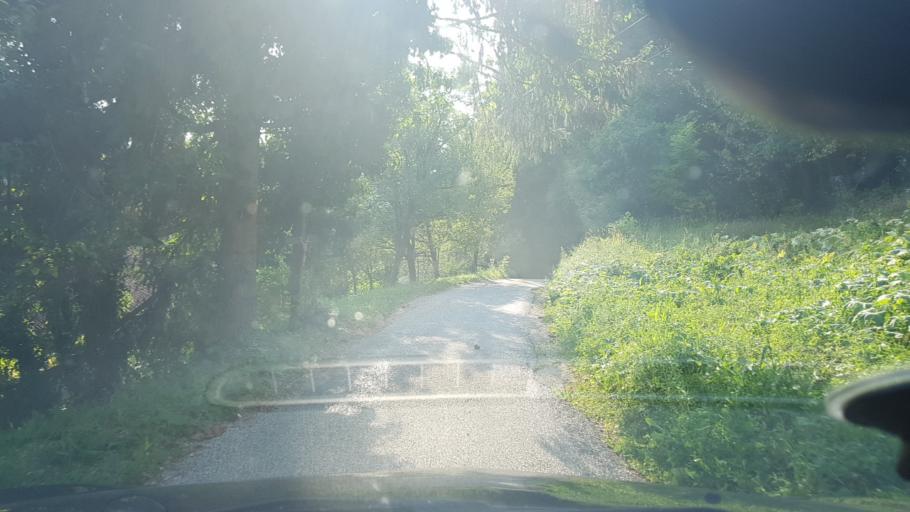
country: HR
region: Krapinsko-Zagorska
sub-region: Grad Krapina
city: Krapina
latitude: 46.1786
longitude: 15.8865
